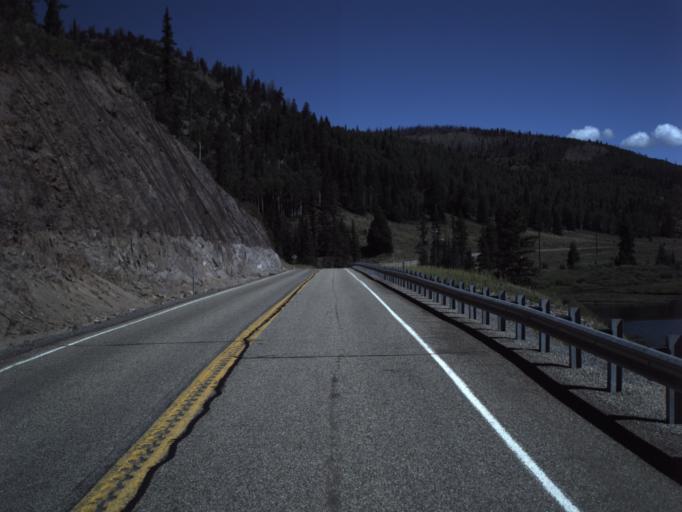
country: US
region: Utah
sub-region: Beaver County
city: Beaver
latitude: 38.2871
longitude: -112.4446
